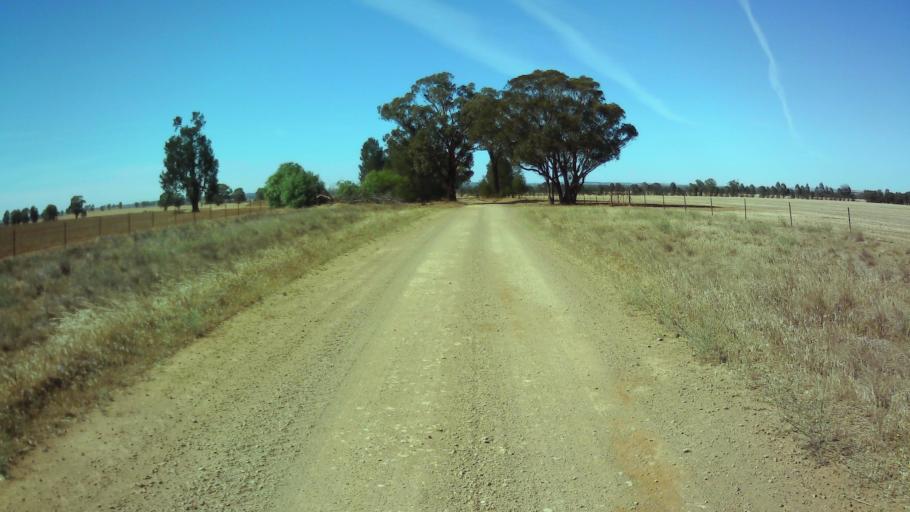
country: AU
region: New South Wales
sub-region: Weddin
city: Grenfell
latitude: -34.0631
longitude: 148.1705
